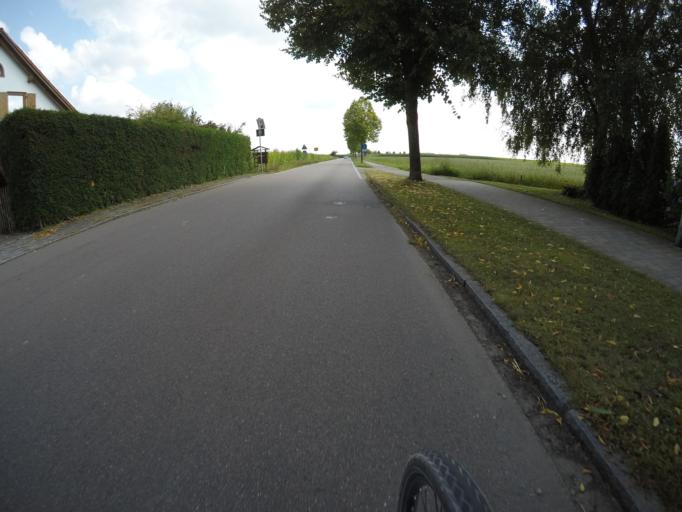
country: DE
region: Bavaria
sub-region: Swabia
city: Westendorf
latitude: 48.5675
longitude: 10.8406
